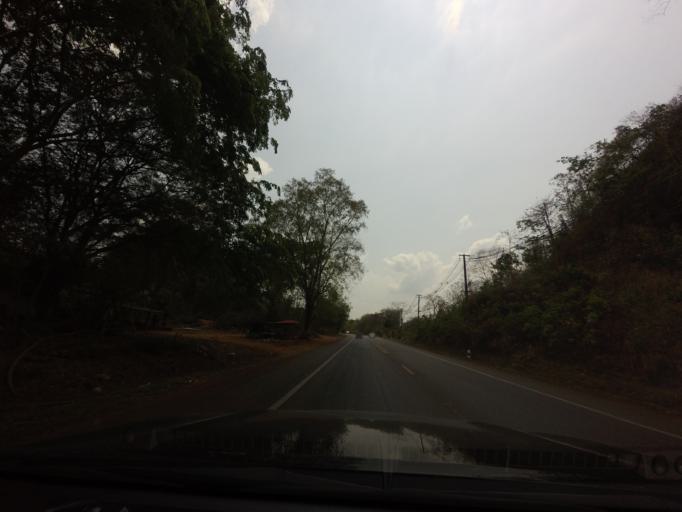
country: TH
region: Kanchanaburi
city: Sai Yok
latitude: 14.1405
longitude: 99.1482
